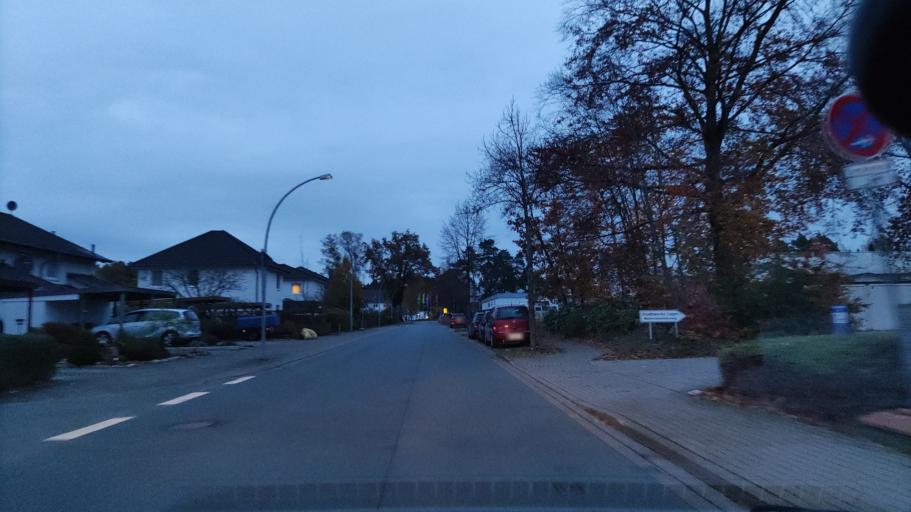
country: DE
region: Lower Saxony
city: Munster
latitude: 52.9977
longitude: 10.1140
